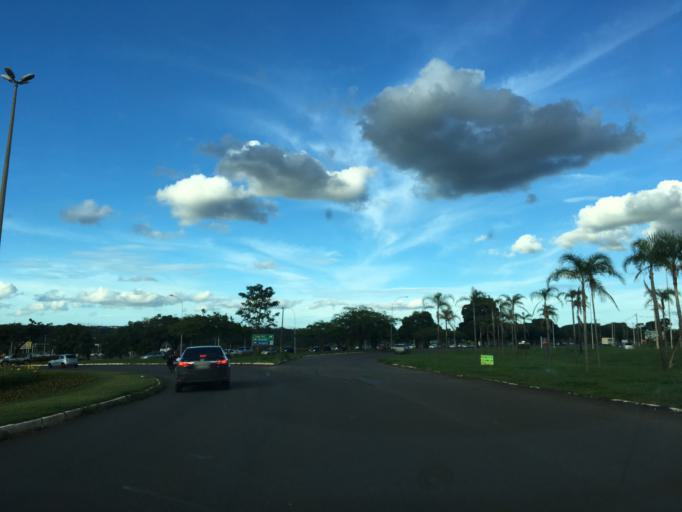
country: BR
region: Federal District
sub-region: Brasilia
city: Brasilia
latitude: -15.8614
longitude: -47.9344
